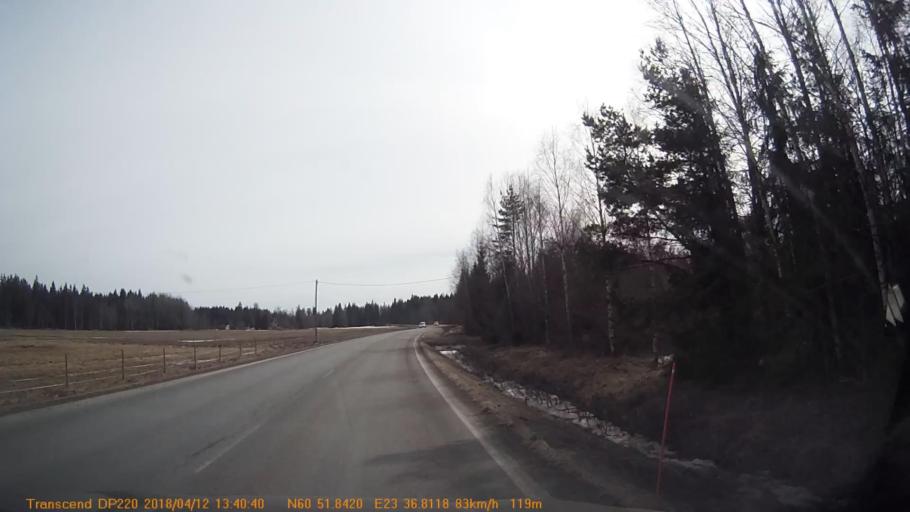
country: FI
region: Haeme
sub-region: Forssa
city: Forssa
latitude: 60.8634
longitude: 23.6138
